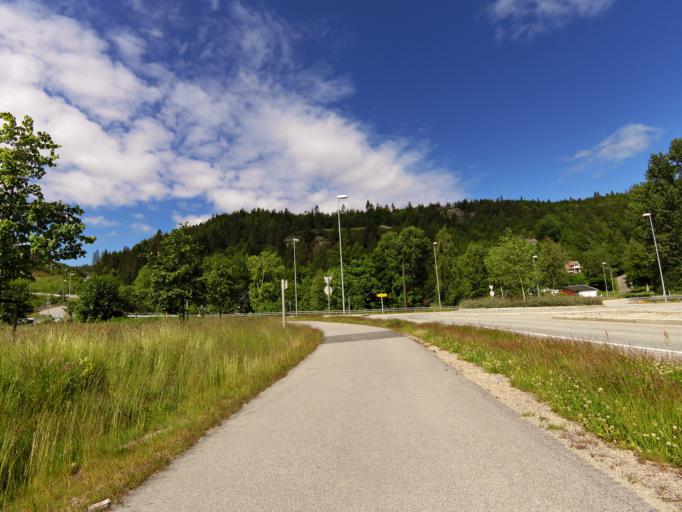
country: NO
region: Vest-Agder
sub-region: Vennesla
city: Vennesla
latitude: 58.2683
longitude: 7.9550
